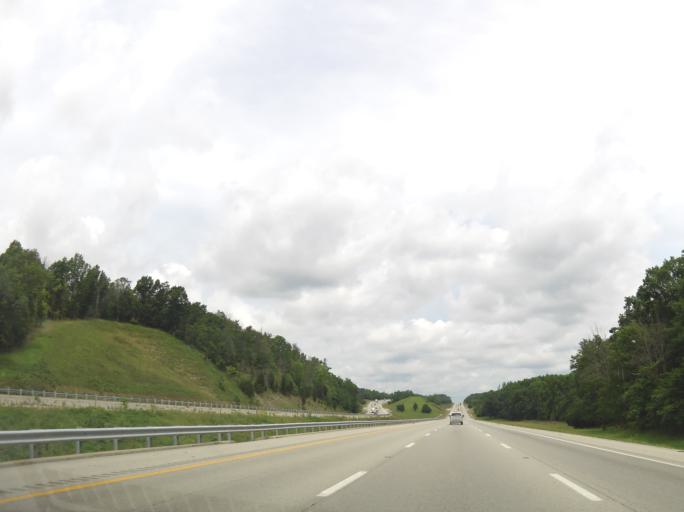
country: US
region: Kentucky
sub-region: Grant County
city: Williamstown
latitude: 38.4458
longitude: -84.5709
